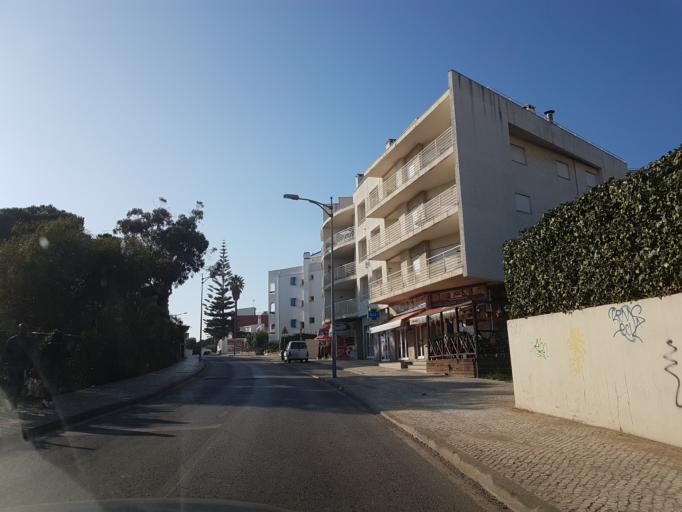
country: PT
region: Faro
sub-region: Albufeira
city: Albufeira
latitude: 37.0896
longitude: -8.2243
